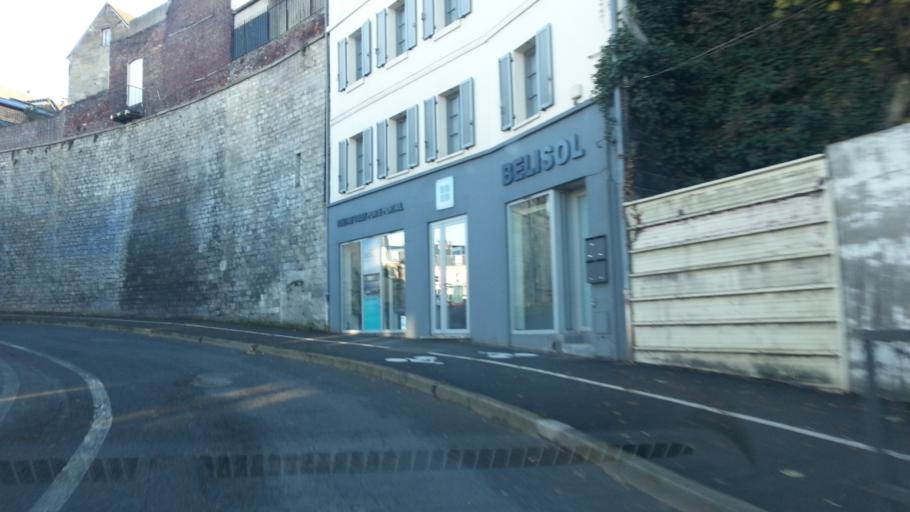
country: FR
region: Picardie
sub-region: Departement de l'Oise
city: Chantilly
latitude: 49.1948
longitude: 2.4640
